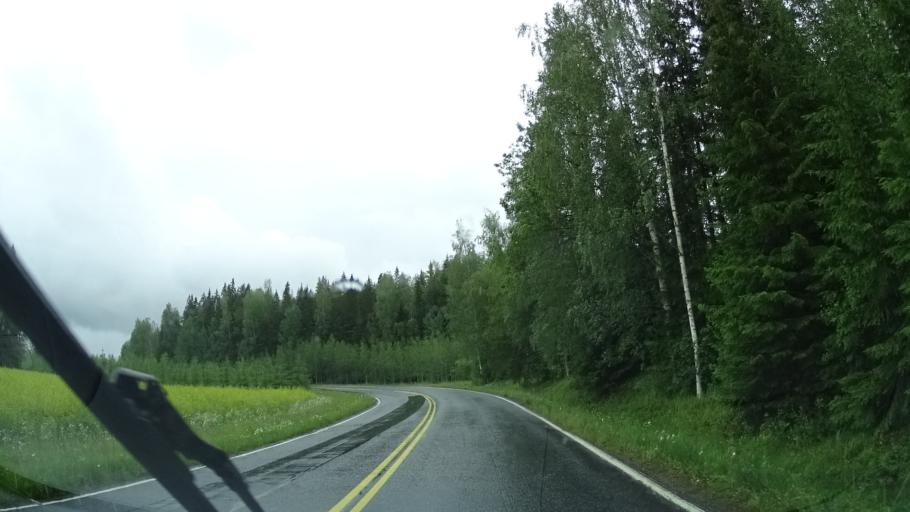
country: FI
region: Haeme
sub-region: Forssa
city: Humppila
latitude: 60.9914
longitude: 23.2568
